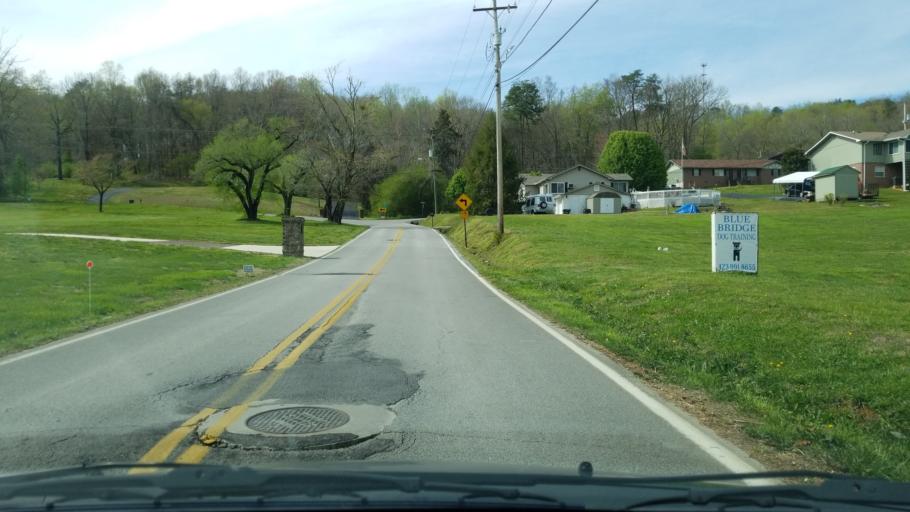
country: US
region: Tennessee
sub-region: Hamilton County
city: Falling Water
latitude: 35.1739
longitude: -85.2596
